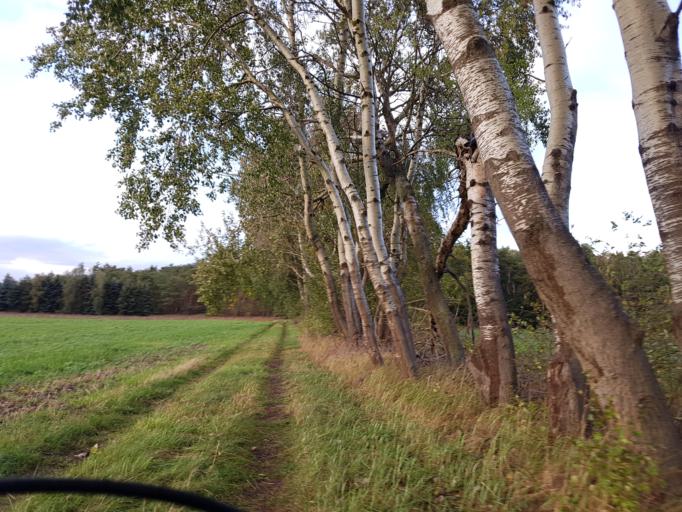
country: DE
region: Brandenburg
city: Bad Liebenwerda
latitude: 51.5430
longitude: 13.4265
